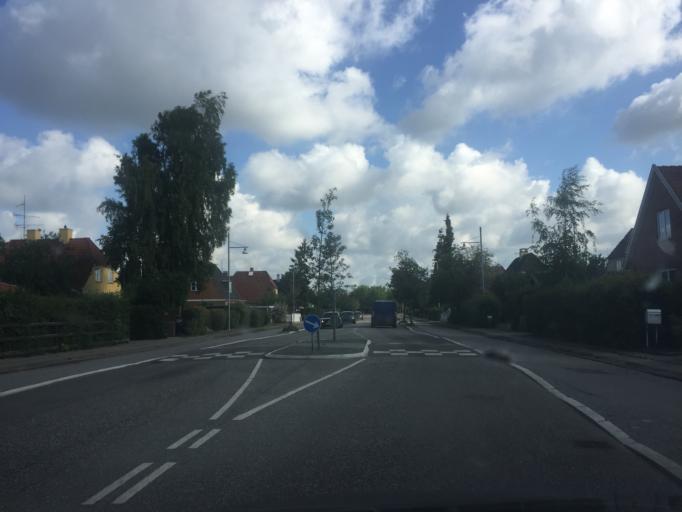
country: DK
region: Capital Region
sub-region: Glostrup Kommune
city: Glostrup
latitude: 55.6711
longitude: 12.4003
